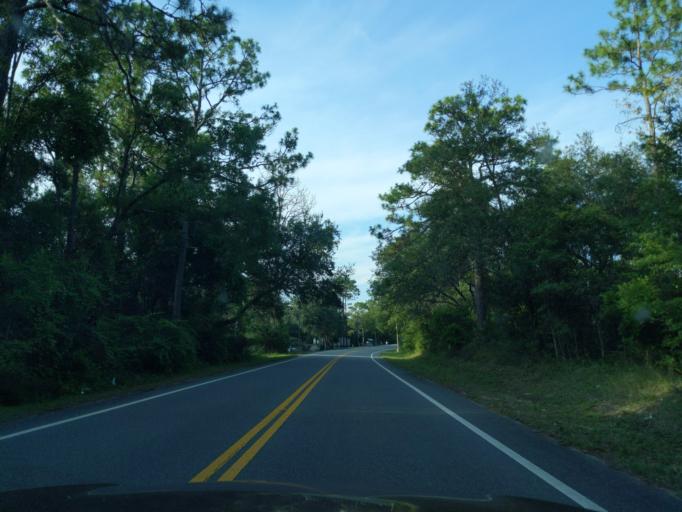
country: US
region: Florida
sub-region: Leon County
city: Tallahassee
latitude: 30.3718
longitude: -84.3616
